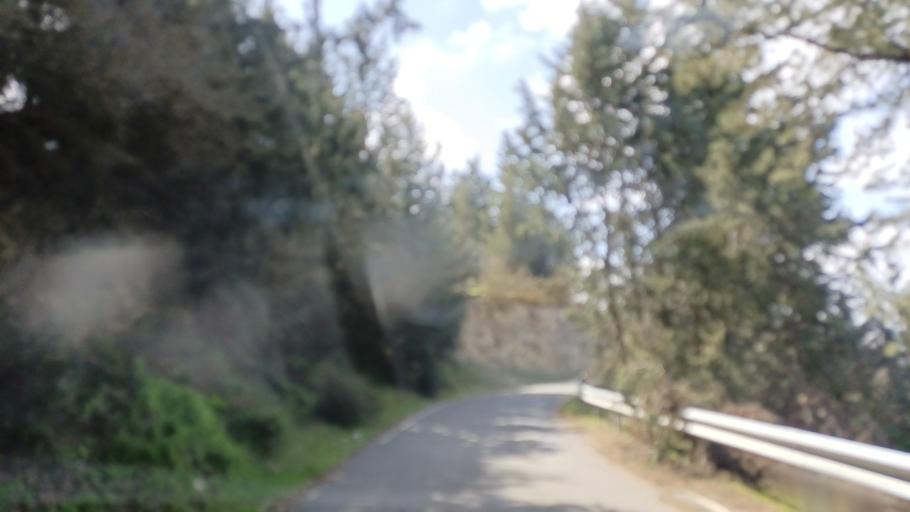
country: CY
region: Limassol
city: Pachna
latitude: 34.8666
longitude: 32.7547
